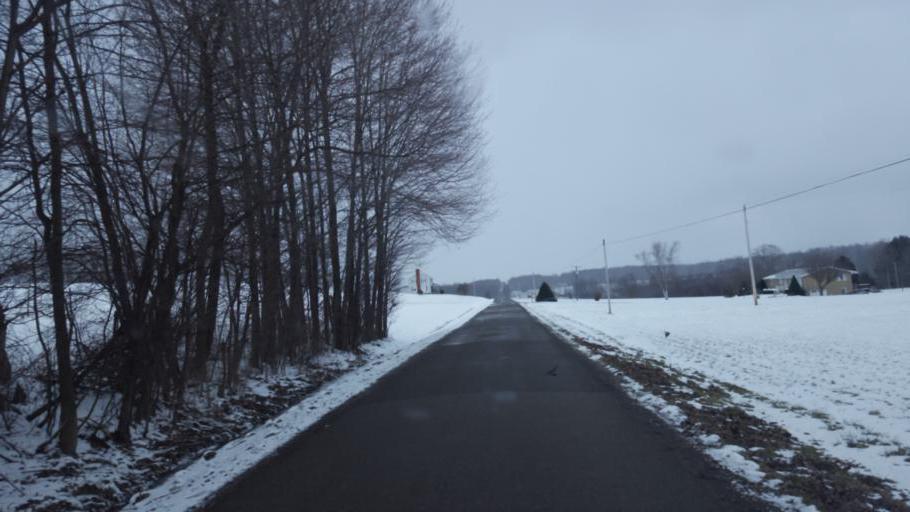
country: US
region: Pennsylvania
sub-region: Mercer County
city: Stoneboro
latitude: 41.4180
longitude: -80.0944
